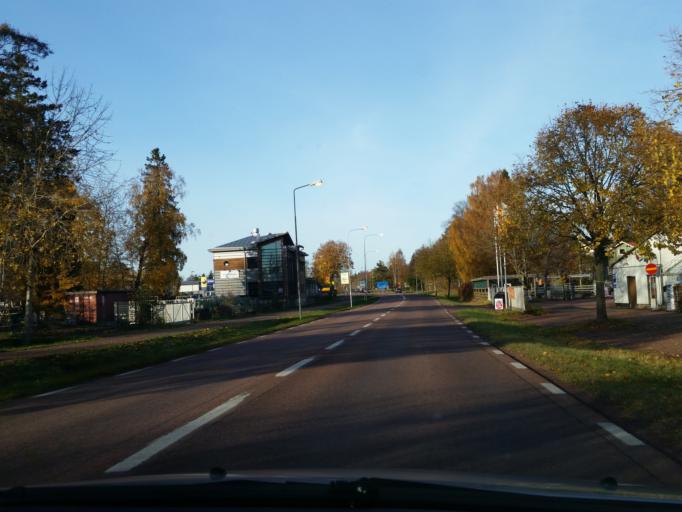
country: AX
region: Mariehamns stad
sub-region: Mariehamn
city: Mariehamn
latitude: 60.1095
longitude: 19.9305
